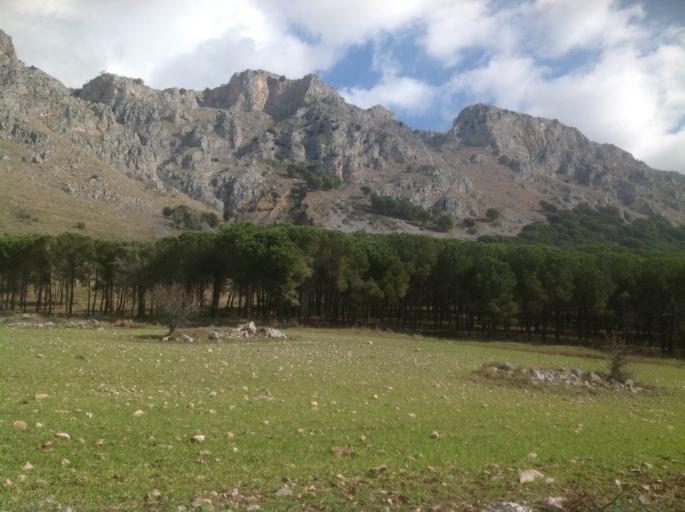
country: IT
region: Calabria
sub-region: Provincia di Cosenza
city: Frascineto
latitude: 39.8384
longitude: 16.2636
